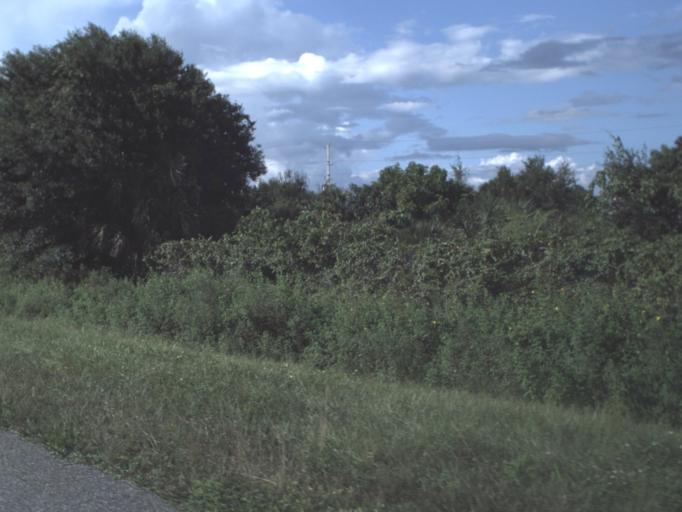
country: US
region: Florida
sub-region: Charlotte County
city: Punta Gorda
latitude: 26.9421
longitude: -82.0318
